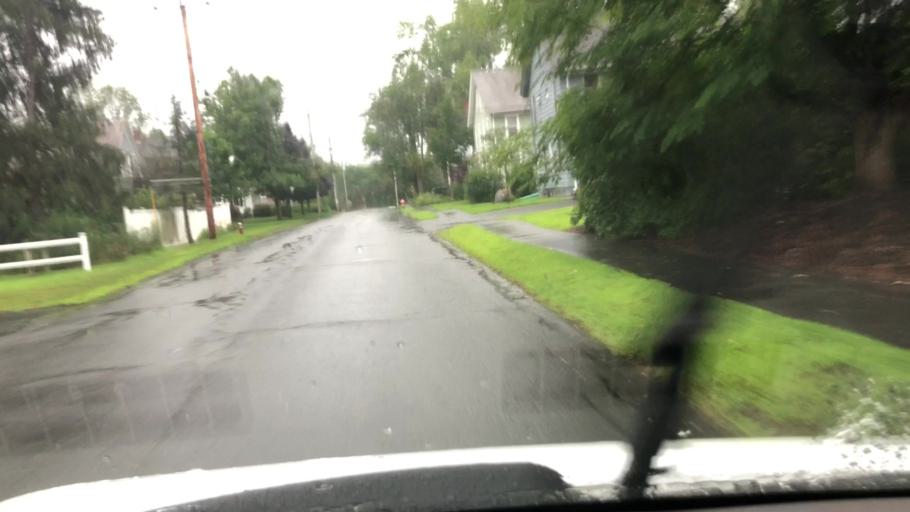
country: US
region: Massachusetts
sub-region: Hampshire County
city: Northampton
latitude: 42.3342
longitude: -72.6548
